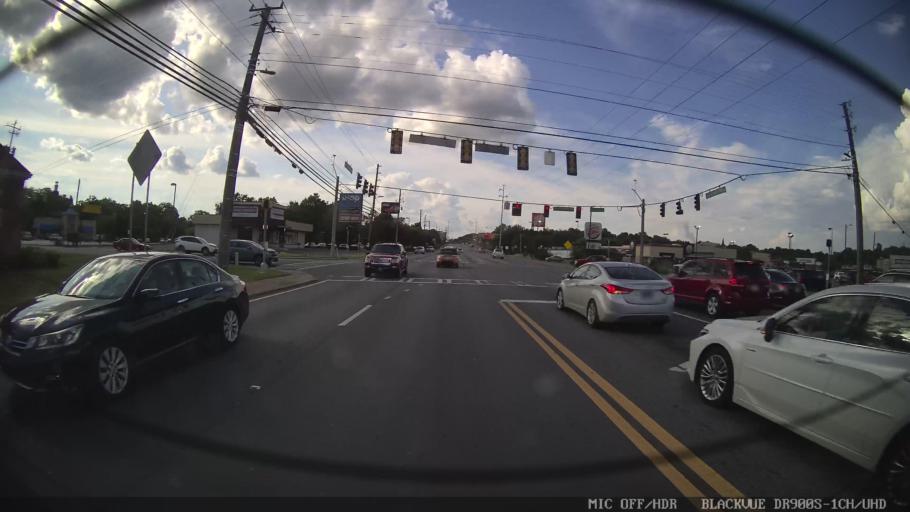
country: US
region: Georgia
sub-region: Floyd County
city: Rome
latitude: 34.2520
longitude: -85.1634
